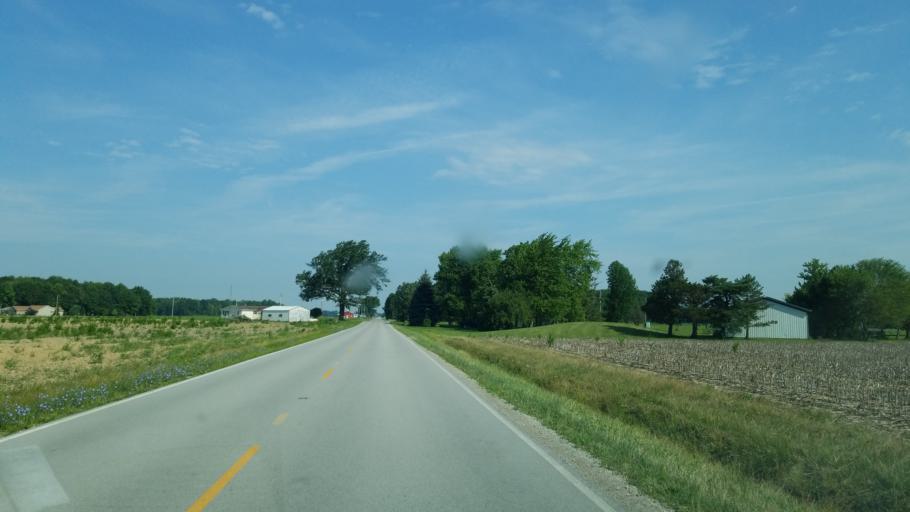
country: US
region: Ohio
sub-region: Huron County
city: Willard
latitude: 41.0211
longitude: -82.8637
